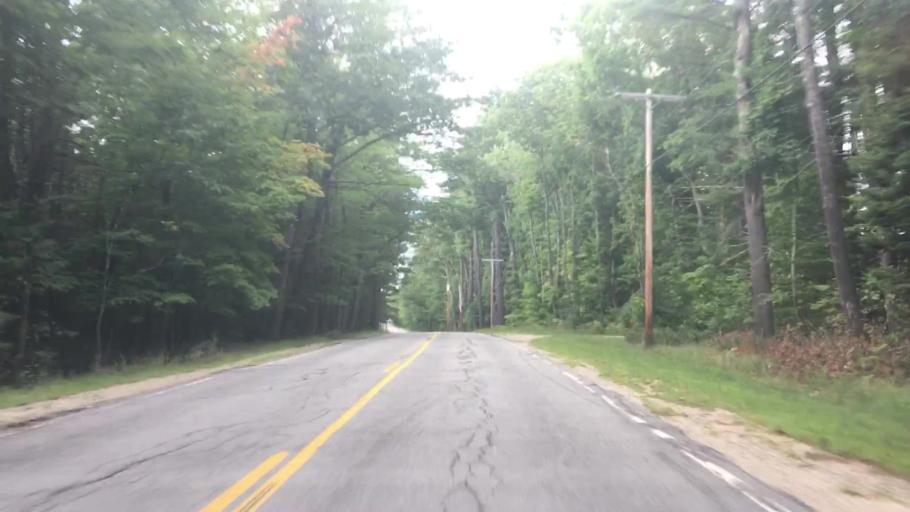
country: US
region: Maine
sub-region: Oxford County
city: Oxford
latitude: 44.0332
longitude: -70.5334
